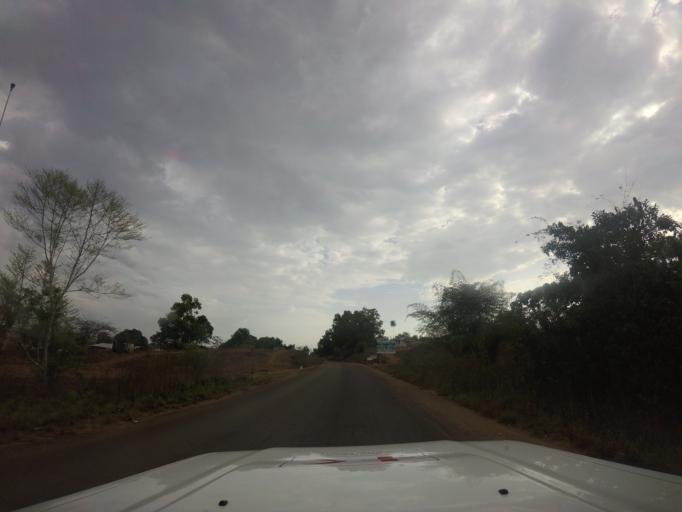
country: LR
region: Grand Cape Mount
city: Robertsport
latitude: 6.8139
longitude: -11.1378
